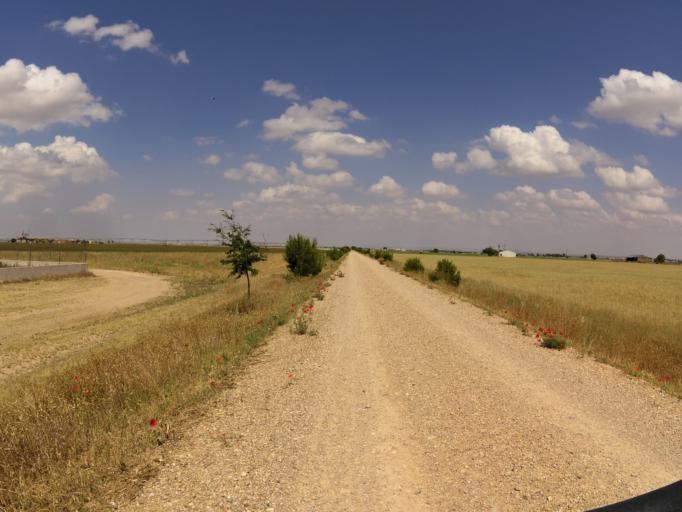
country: ES
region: Castille-La Mancha
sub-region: Provincia de Albacete
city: Pozuelo
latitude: 38.9095
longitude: -2.0273
